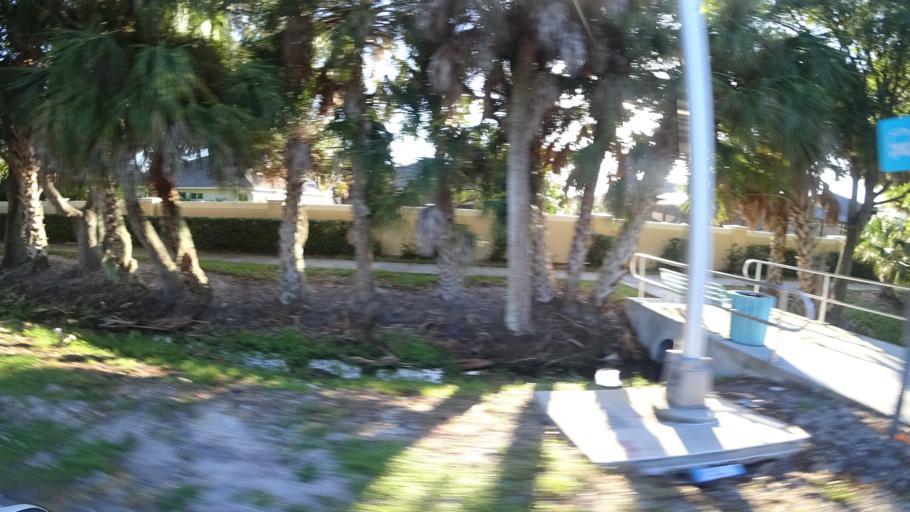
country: US
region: Florida
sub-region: Manatee County
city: Samoset
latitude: 27.4645
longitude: -82.5260
